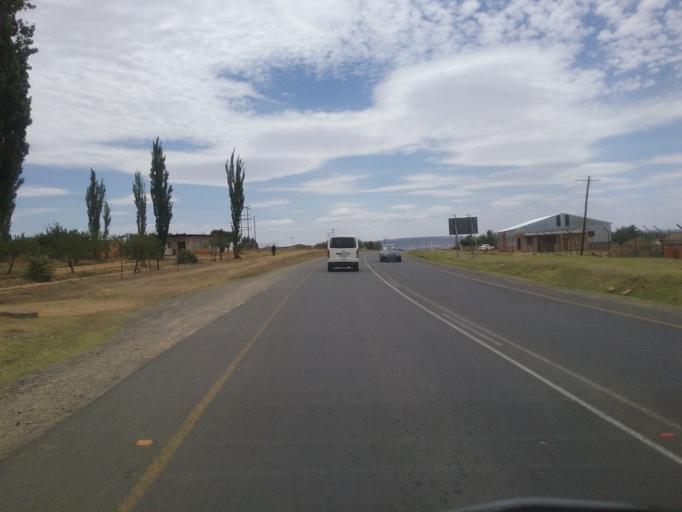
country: LS
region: Maseru
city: Maseru
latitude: -29.4832
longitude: 27.5267
